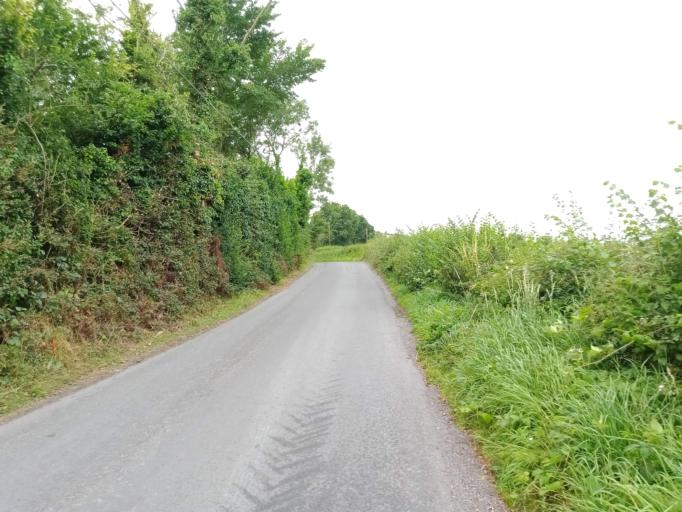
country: IE
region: Leinster
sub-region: Kilkenny
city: Ballyragget
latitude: 52.8090
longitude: -7.4322
